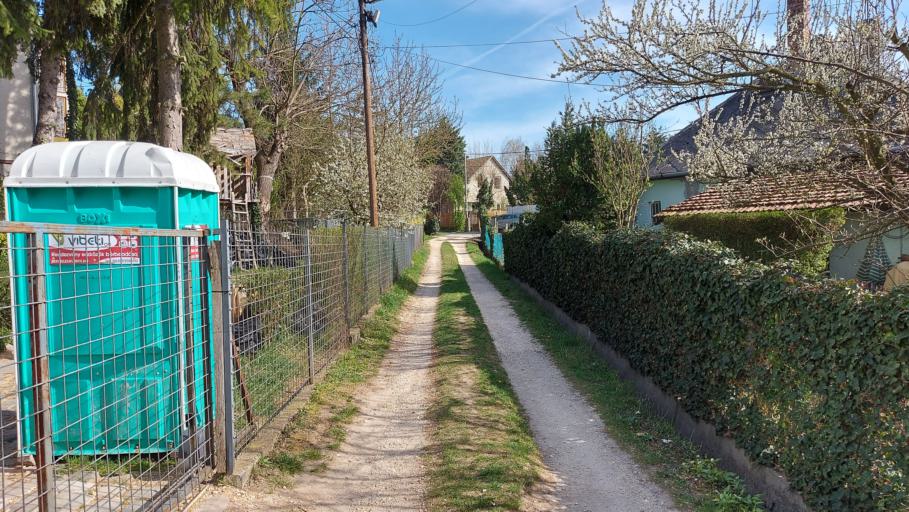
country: HU
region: Pest
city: Budaors
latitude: 47.4381
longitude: 18.9742
